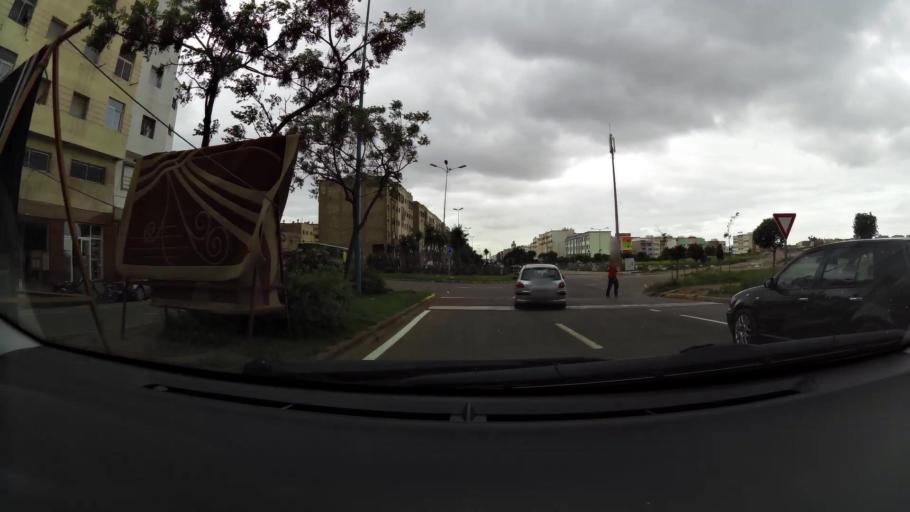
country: MA
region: Grand Casablanca
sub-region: Mediouna
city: Tit Mellil
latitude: 33.5719
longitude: -7.5398
